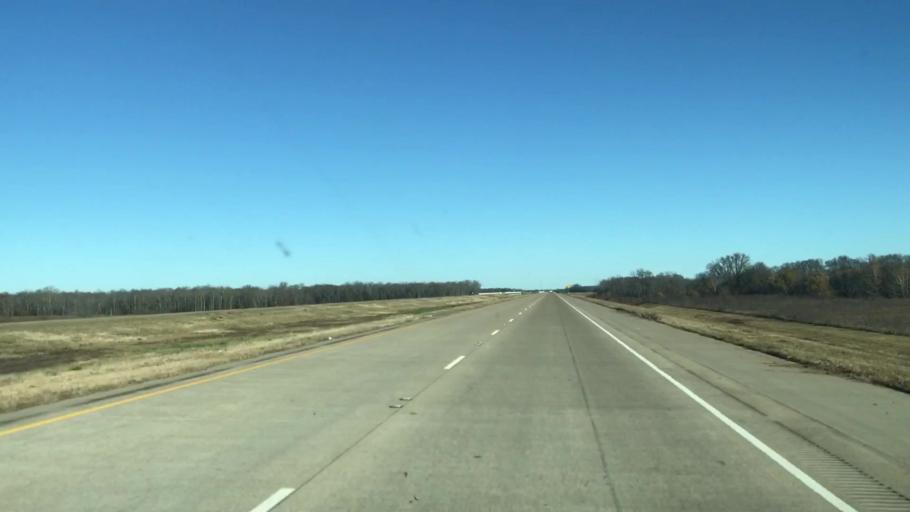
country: US
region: Louisiana
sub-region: Caddo Parish
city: Blanchard
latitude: 32.6189
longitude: -93.8353
